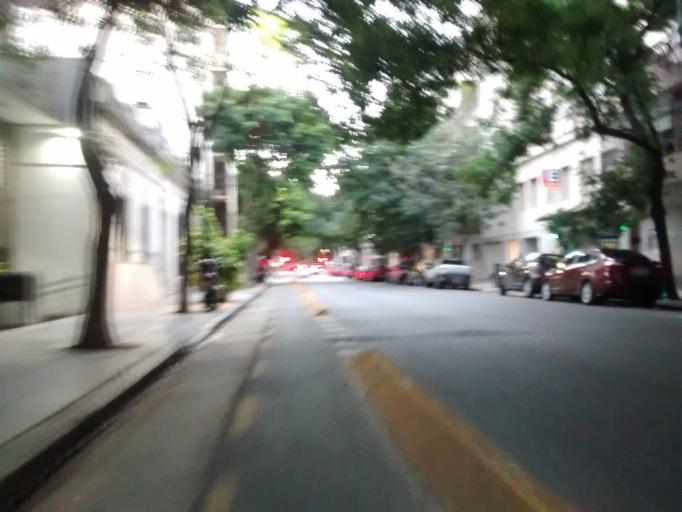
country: AR
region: Buenos Aires F.D.
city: Villa Santa Rita
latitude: -34.6049
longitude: -58.4527
